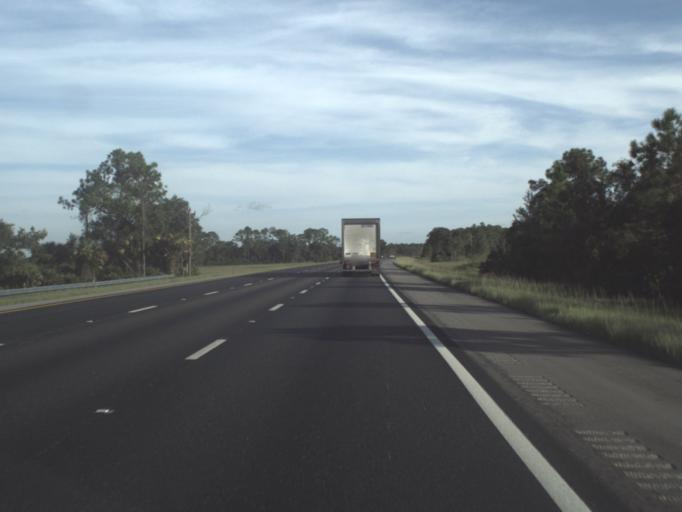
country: US
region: Florida
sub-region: Lee County
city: Suncoast Estates
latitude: 26.7948
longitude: -81.9105
